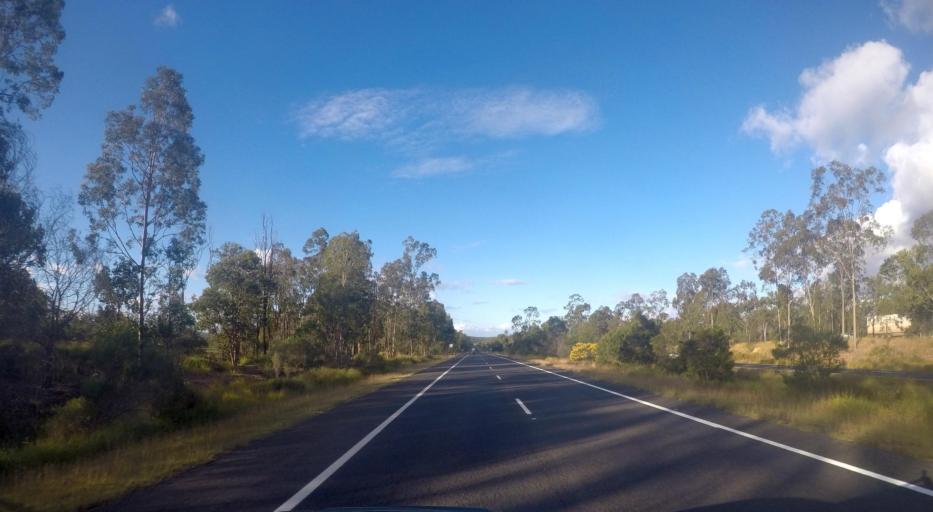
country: AU
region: Queensland
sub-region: Lockyer Valley
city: Gatton
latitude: -27.5436
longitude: 152.2329
